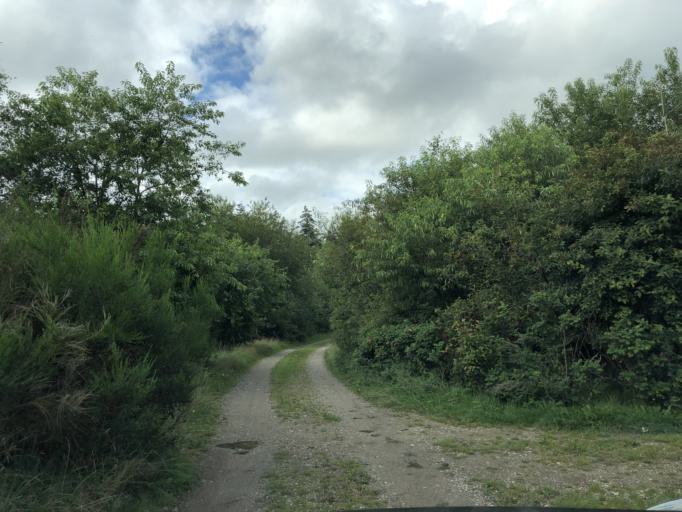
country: DK
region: Central Jutland
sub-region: Holstebro Kommune
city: Ulfborg
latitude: 56.2526
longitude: 8.3882
